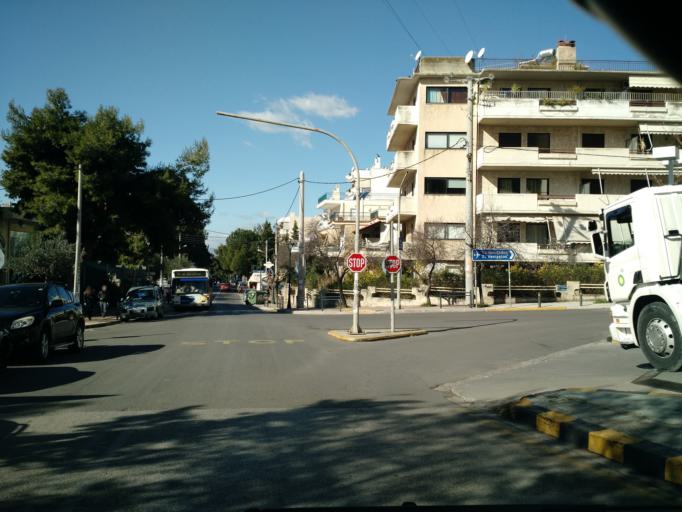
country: GR
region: Attica
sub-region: Nomarchia Athinas
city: Cholargos
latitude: 37.9994
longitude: 23.8174
